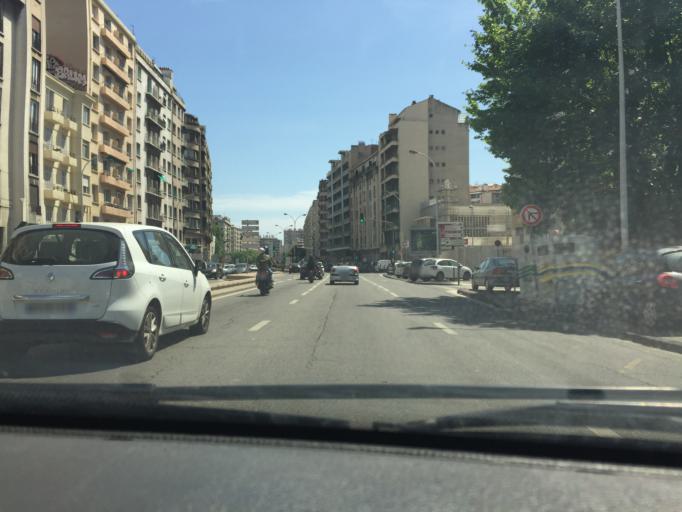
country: FR
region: Provence-Alpes-Cote d'Azur
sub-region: Departement des Bouches-du-Rhone
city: Marseille 04
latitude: 43.3027
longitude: 5.4006
